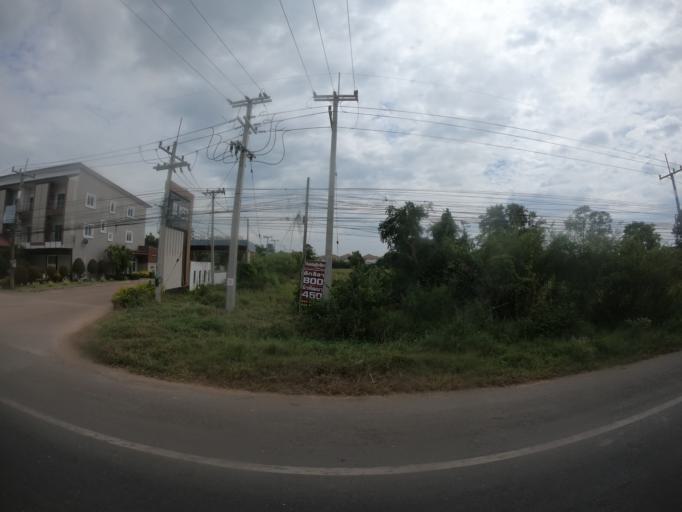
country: TH
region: Maha Sarakham
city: Maha Sarakham
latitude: 16.2535
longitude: 103.2765
